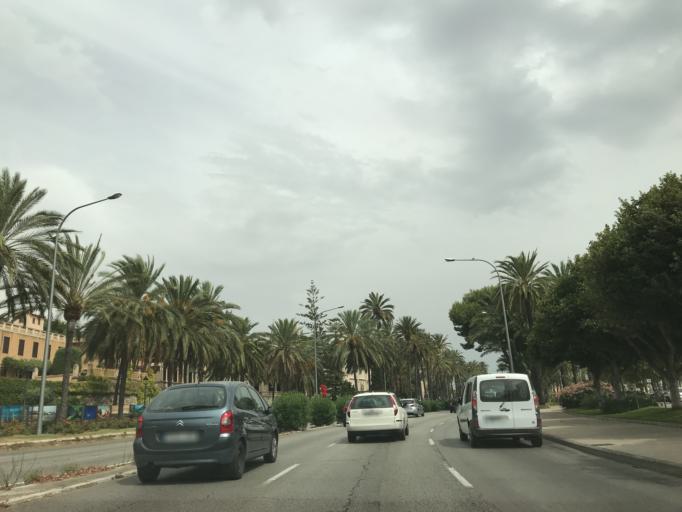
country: ES
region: Balearic Islands
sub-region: Illes Balears
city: Palma
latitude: 39.5691
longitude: 2.6420
